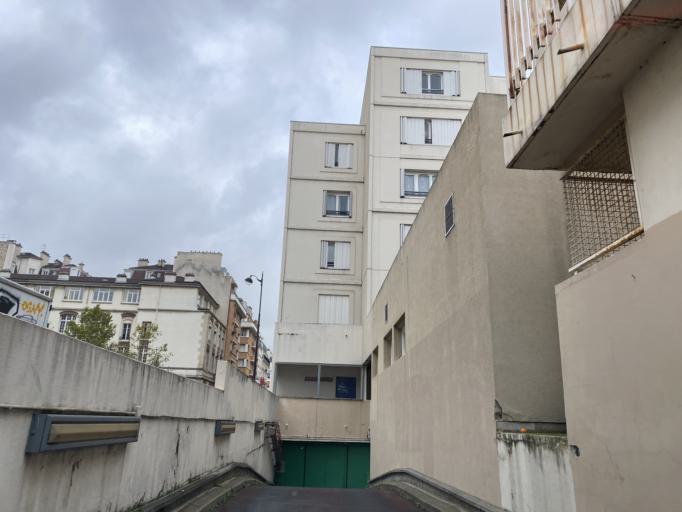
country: FR
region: Ile-de-France
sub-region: Departement de Seine-Saint-Denis
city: Le Pre-Saint-Gervais
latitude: 48.8601
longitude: 2.3833
